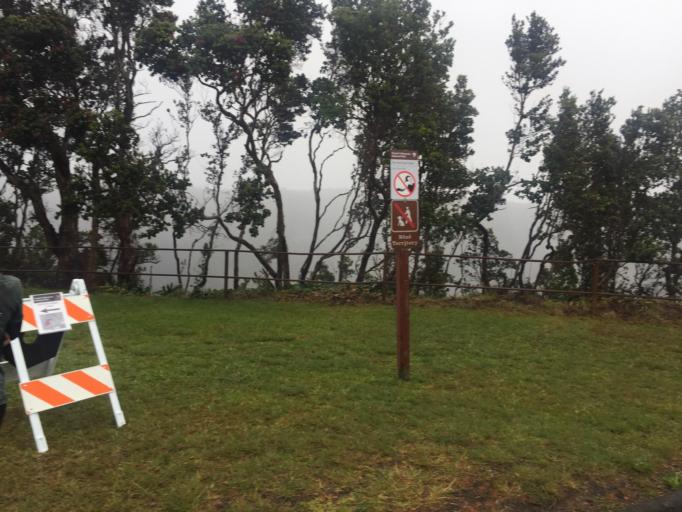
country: US
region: Hawaii
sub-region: Hawaii County
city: Volcano
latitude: 19.4115
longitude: -155.2500
